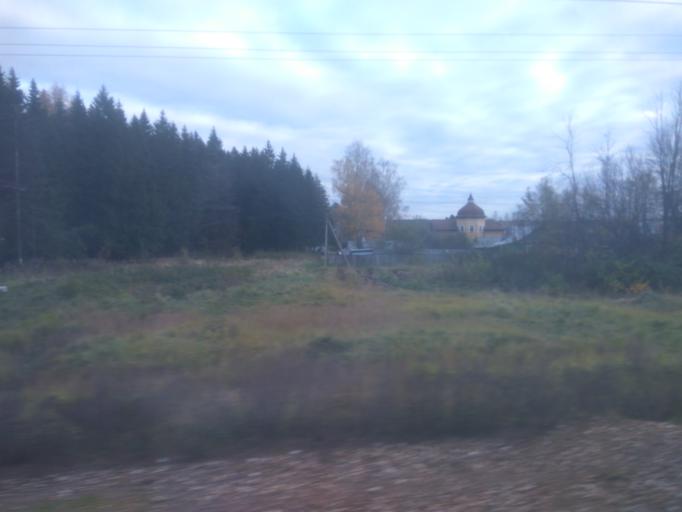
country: RU
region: Moskovskaya
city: Aprelevka
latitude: 55.5729
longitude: 37.0996
